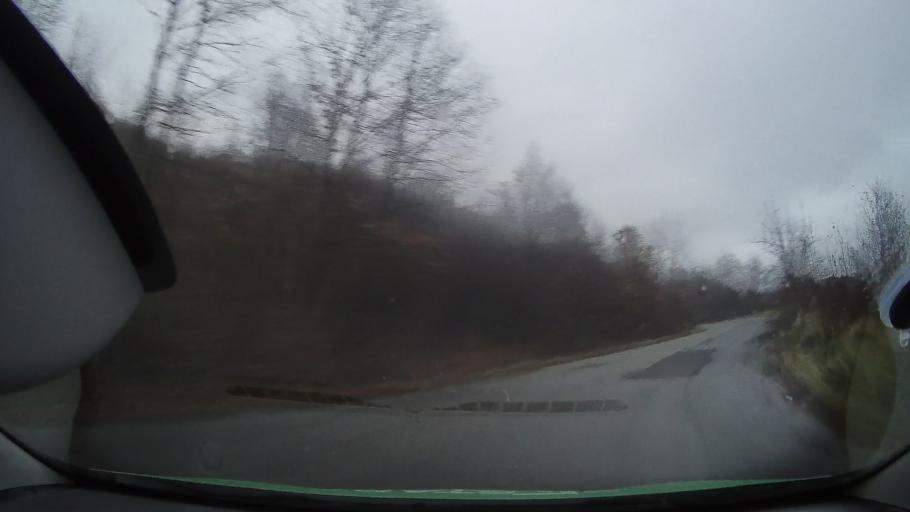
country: RO
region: Hunedoara
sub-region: Comuna Ribita
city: Ribita
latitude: 46.2372
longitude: 22.7437
